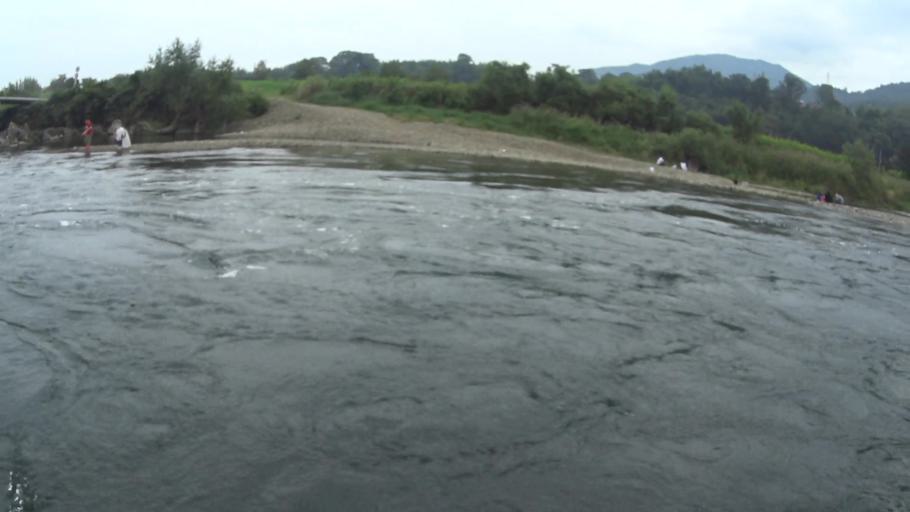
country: JP
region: Kyoto
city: Kameoka
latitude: 35.0179
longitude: 135.5939
